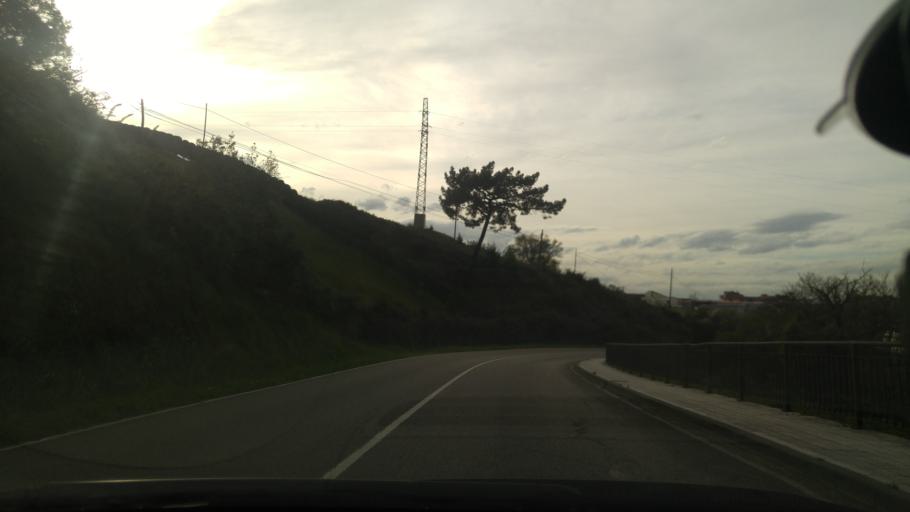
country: ES
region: Asturias
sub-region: Province of Asturias
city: Corvera de Asturias
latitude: 43.5300
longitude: -5.8805
